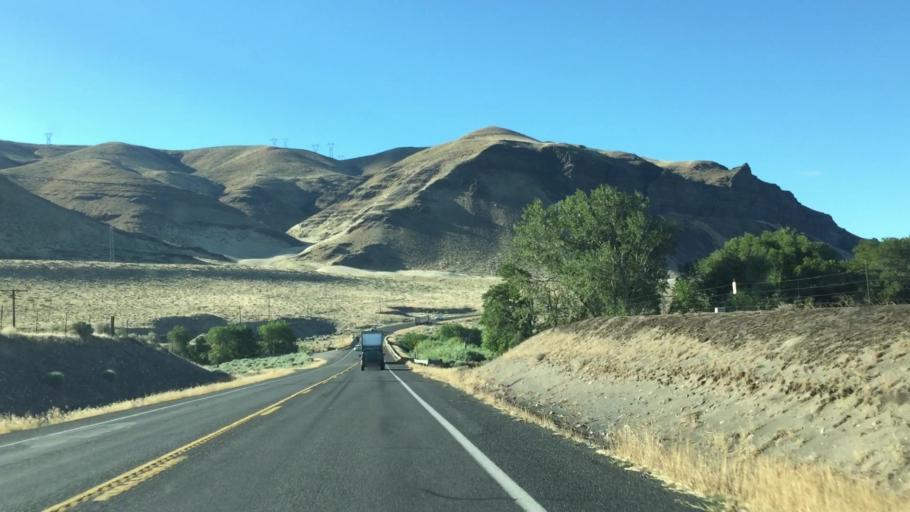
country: US
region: Washington
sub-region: Grant County
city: Mattawa
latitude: 46.8175
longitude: -119.9223
